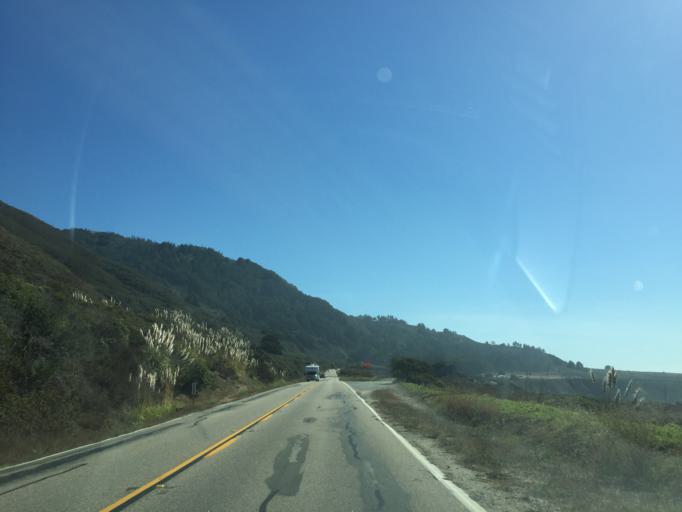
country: US
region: California
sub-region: Monterey County
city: King City
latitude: 35.9297
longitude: -121.4680
